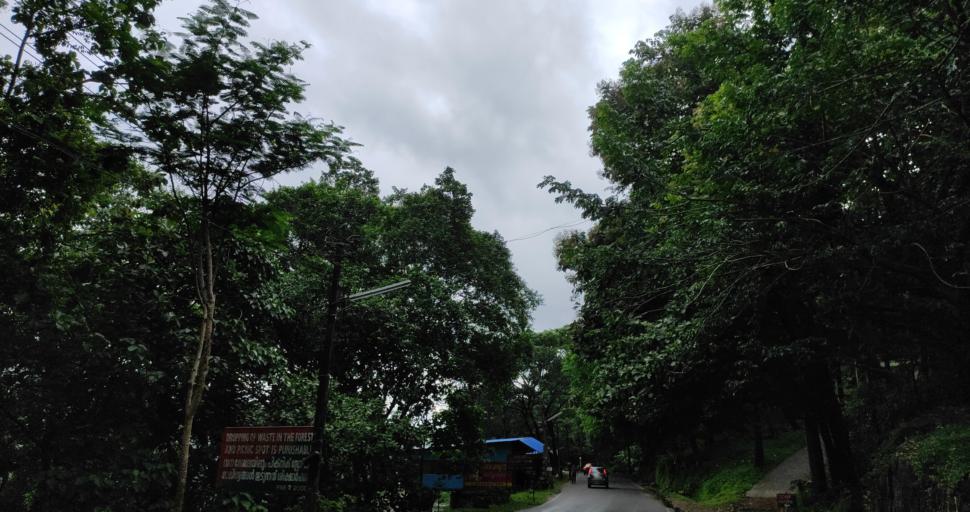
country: IN
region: Kerala
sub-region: Ernakulam
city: Angamali
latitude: 10.2883
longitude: 76.5652
